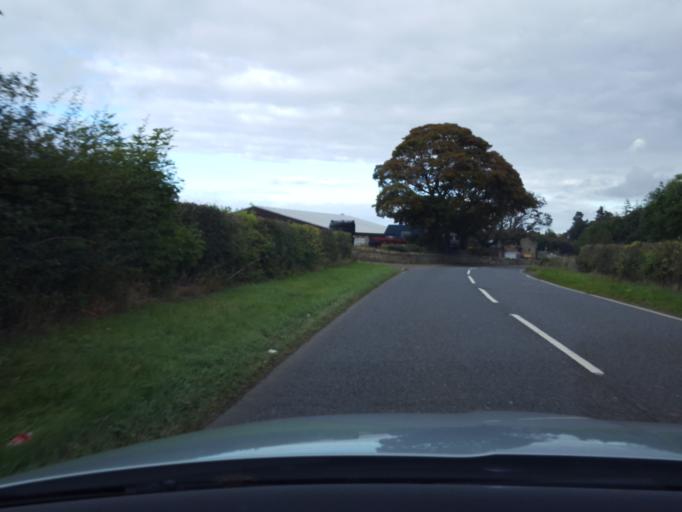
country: GB
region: Scotland
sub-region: Fife
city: Pathhead
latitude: 55.8752
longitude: -2.9885
